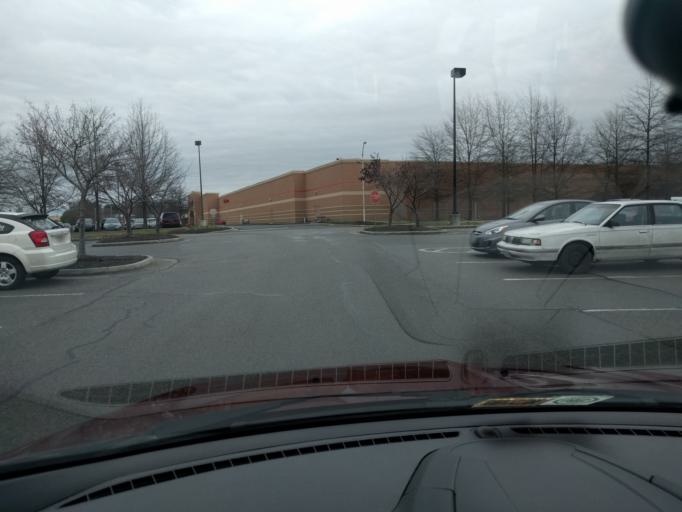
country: US
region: Virginia
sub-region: Montgomery County
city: Christiansburg
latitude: 37.1568
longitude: -80.4241
